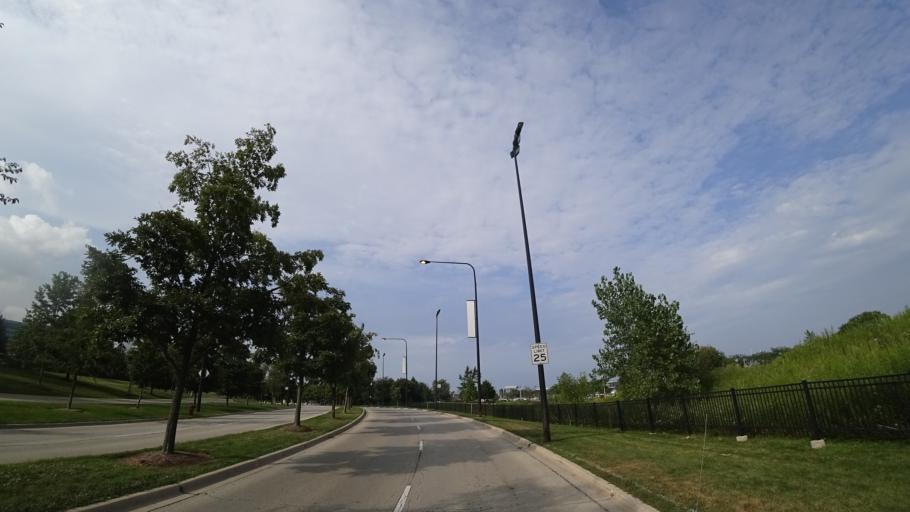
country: US
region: Illinois
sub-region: Cook County
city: Chicago
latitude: 41.8586
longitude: -87.6142
